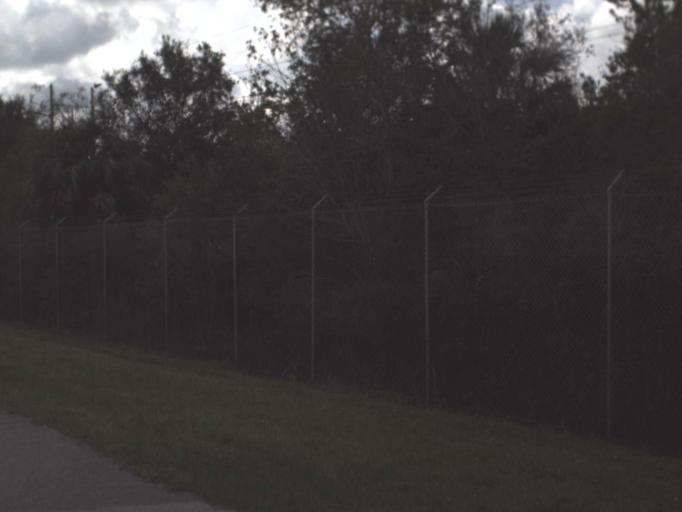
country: US
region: Florida
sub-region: Collier County
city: Lely Resort
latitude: 26.0286
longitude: -81.3451
